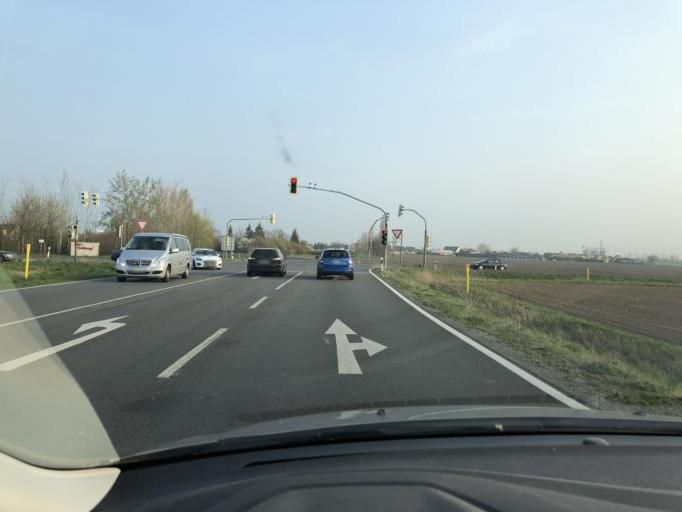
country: DE
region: Saxony
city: Delitzsch
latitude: 51.5249
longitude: 12.3114
